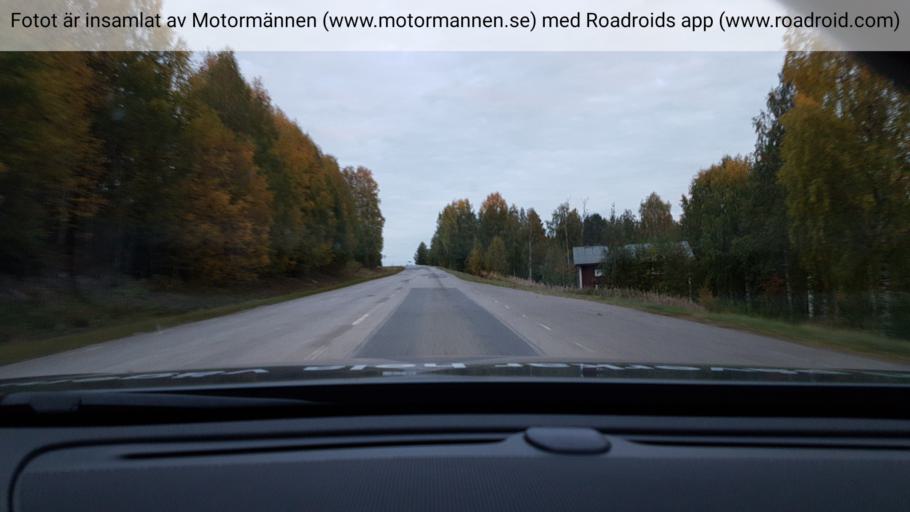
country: SE
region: Norrbotten
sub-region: Alvsbyns Kommun
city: AElvsbyn
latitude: 65.8557
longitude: 20.4298
